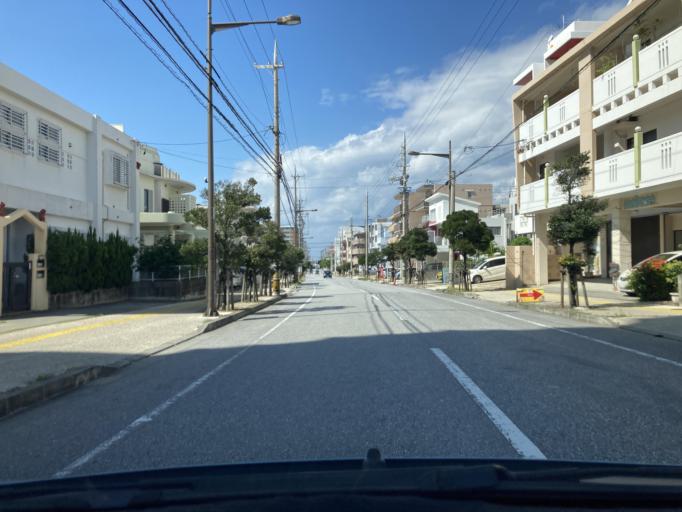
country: JP
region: Okinawa
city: Ginowan
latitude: 26.2724
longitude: 127.7341
